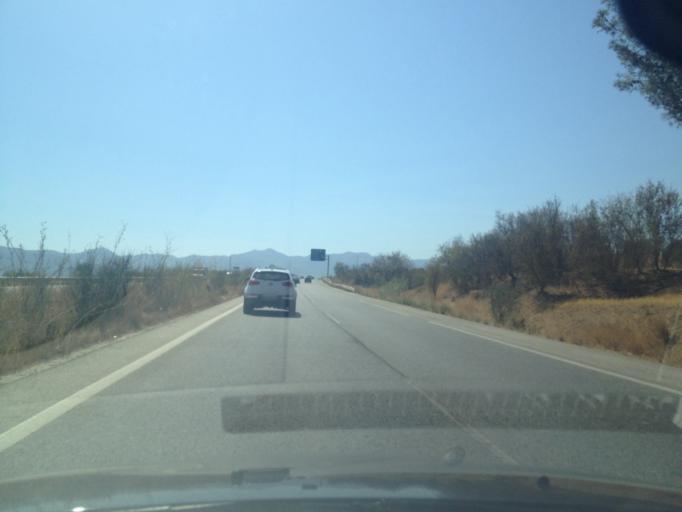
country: ES
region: Andalusia
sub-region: Provincia de Malaga
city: Alhaurin de la Torre
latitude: 36.7246
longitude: -4.5529
